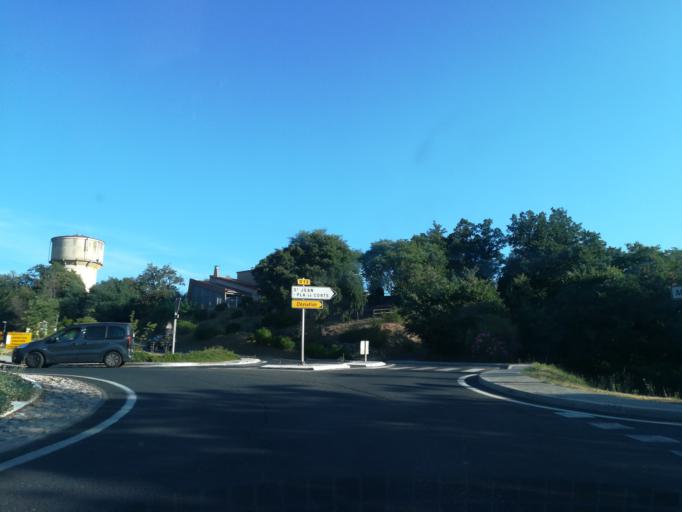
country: FR
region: Languedoc-Roussillon
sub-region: Departement des Pyrenees-Orientales
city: Maureillas-las-Illas
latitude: 42.4902
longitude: 2.8031
